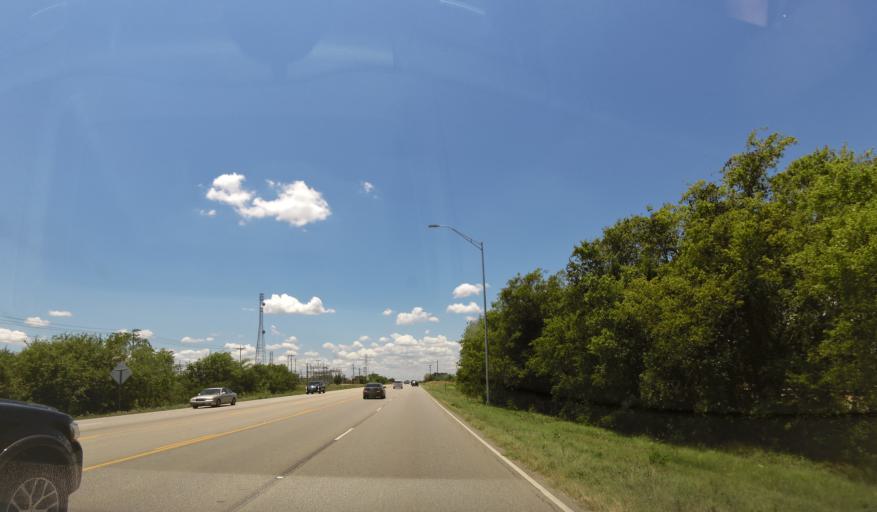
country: US
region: Texas
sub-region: Lee County
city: Giddings
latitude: 30.1848
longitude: -96.9482
